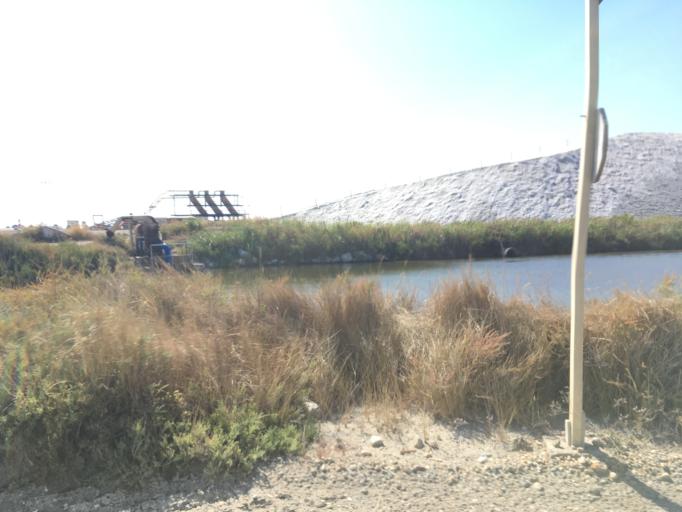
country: FR
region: Languedoc-Roussillon
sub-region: Departement du Gard
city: Aigues-Mortes
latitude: 43.5457
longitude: 4.1879
